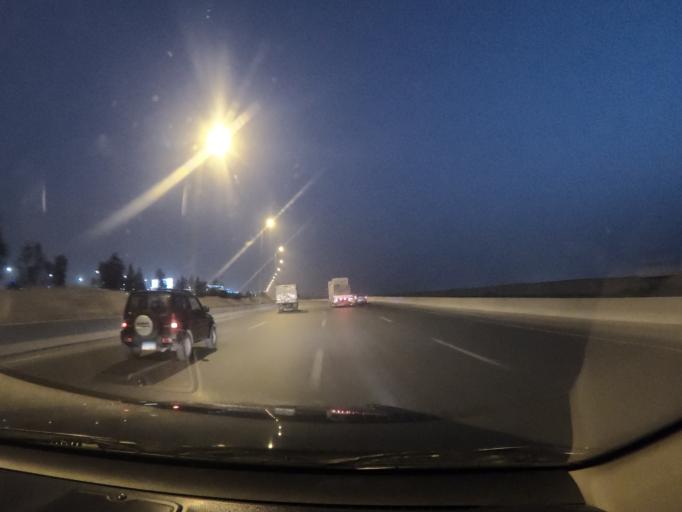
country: EG
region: Muhafazat al Qahirah
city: Cairo
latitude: 30.0284
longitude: 31.4017
